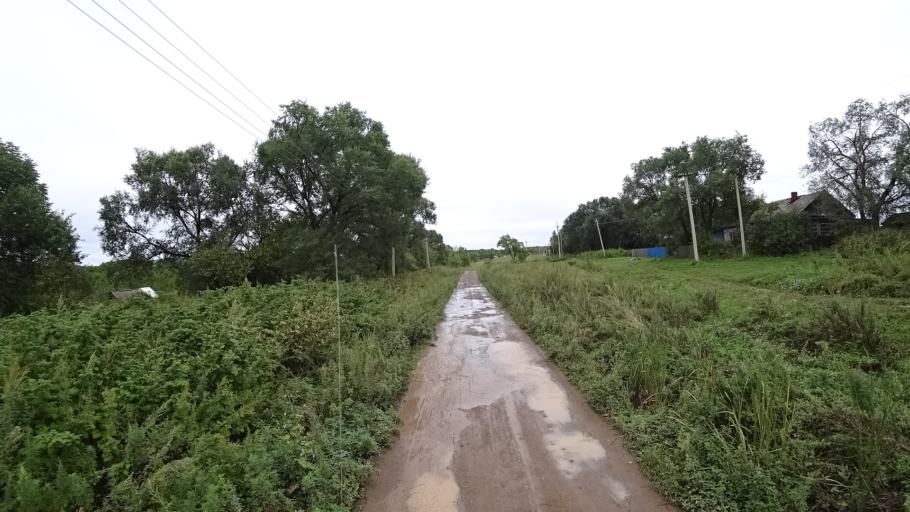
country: RU
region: Primorskiy
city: Rettikhovka
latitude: 44.0568
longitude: 132.6534
